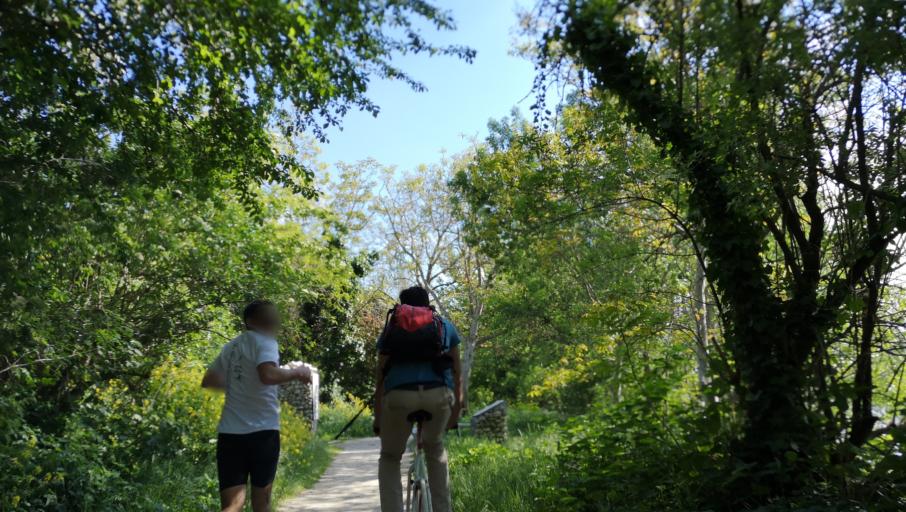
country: FR
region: Midi-Pyrenees
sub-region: Departement de la Haute-Garonne
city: Blagnac
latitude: 43.6364
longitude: 1.4049
